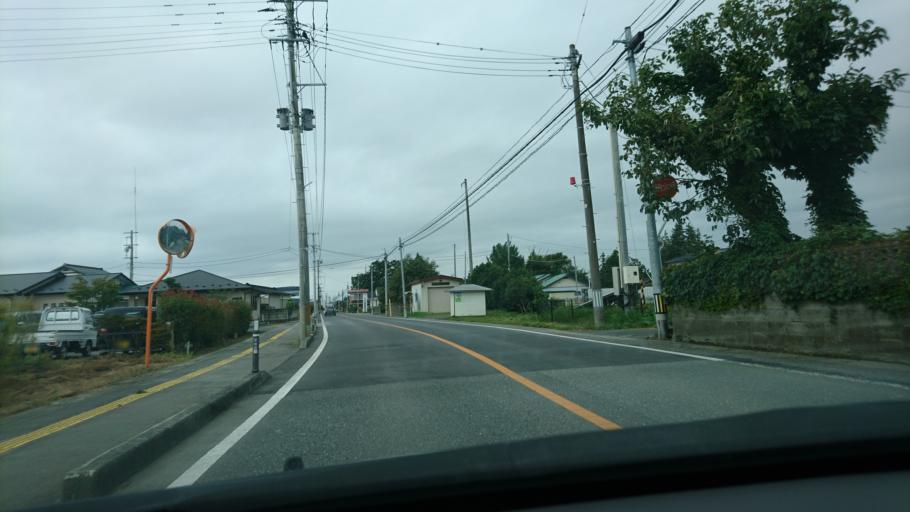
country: JP
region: Iwate
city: Ichinoseki
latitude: 38.7658
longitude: 141.0865
